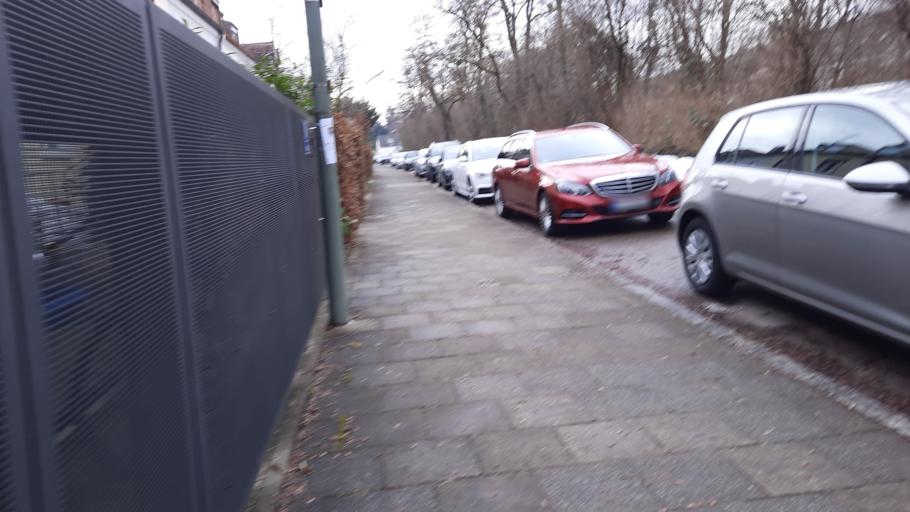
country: DE
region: Bavaria
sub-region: Upper Bavaria
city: Neuried
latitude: 48.1201
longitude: 11.5115
